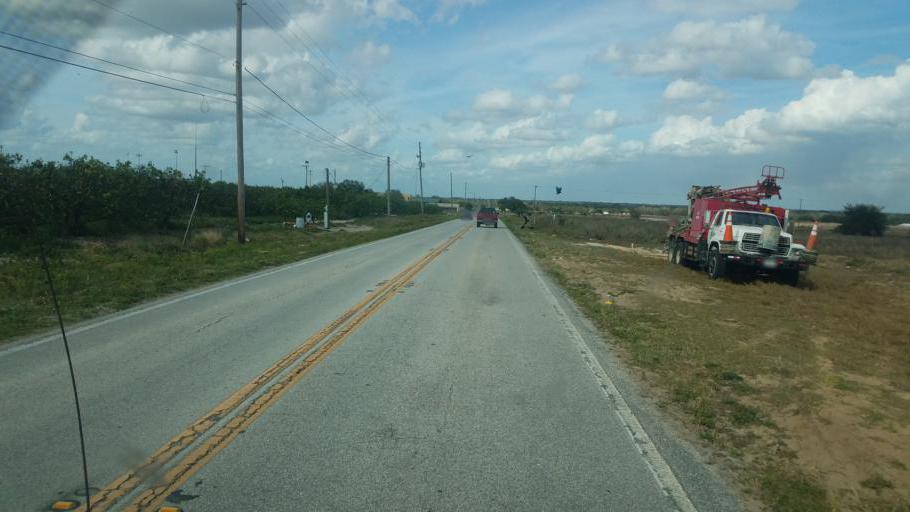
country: US
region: Florida
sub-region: Polk County
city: Haines City
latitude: 28.0934
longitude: -81.6068
